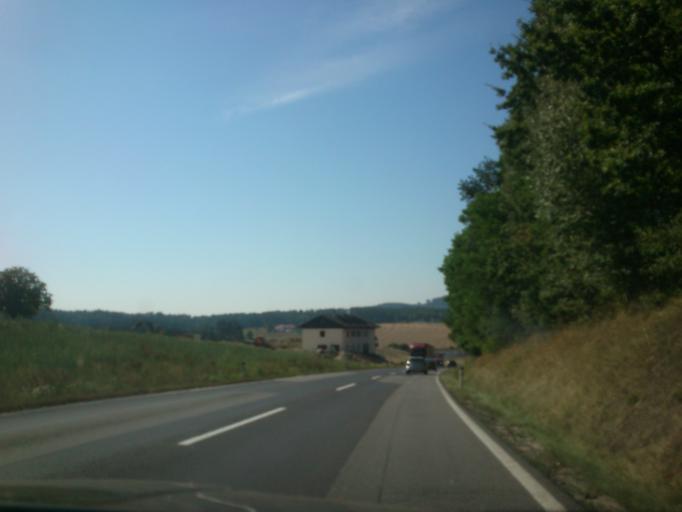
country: AT
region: Upper Austria
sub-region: Politischer Bezirk Freistadt
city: Freistadt
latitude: 48.4662
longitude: 14.5023
